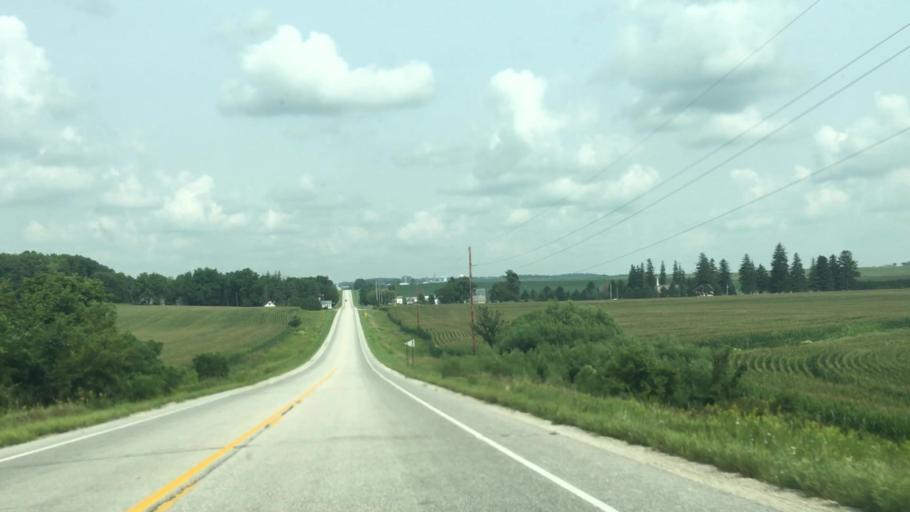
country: US
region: Minnesota
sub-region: Fillmore County
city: Harmony
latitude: 43.5893
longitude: -91.9298
